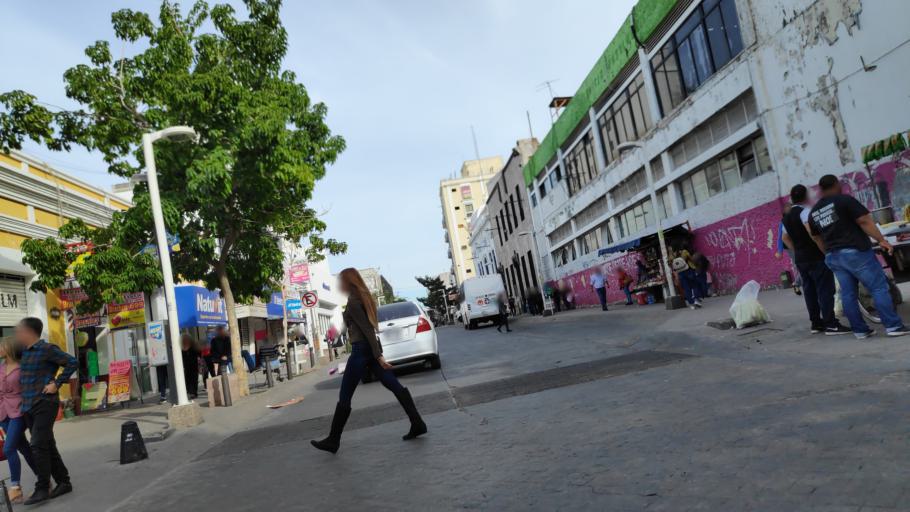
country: MX
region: Sinaloa
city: Culiacan
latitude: 24.8095
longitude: -107.3971
